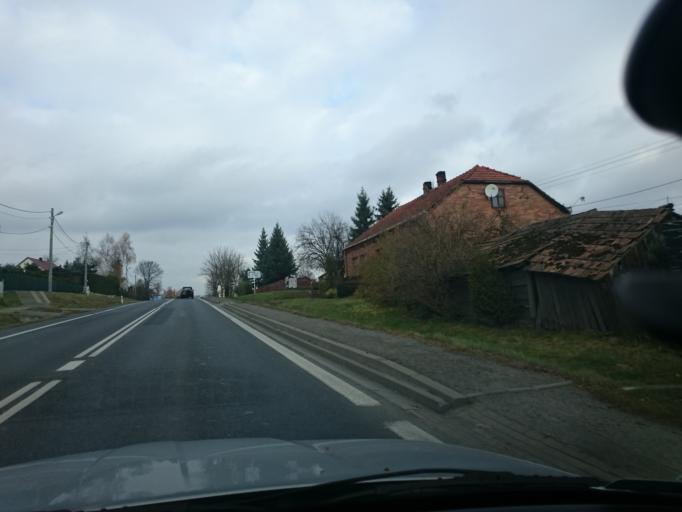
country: PL
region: Lesser Poland Voivodeship
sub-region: Powiat krakowski
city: Michalowice
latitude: 50.1551
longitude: 19.9822
